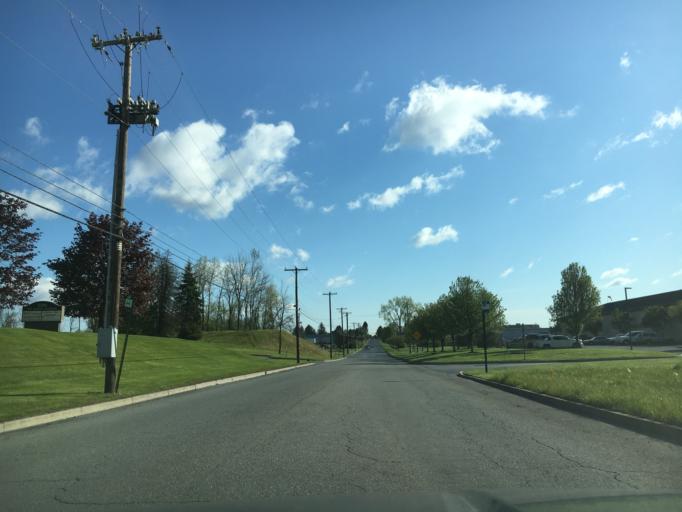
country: US
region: Pennsylvania
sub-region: Lehigh County
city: Stiles
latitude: 40.6732
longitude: -75.5064
